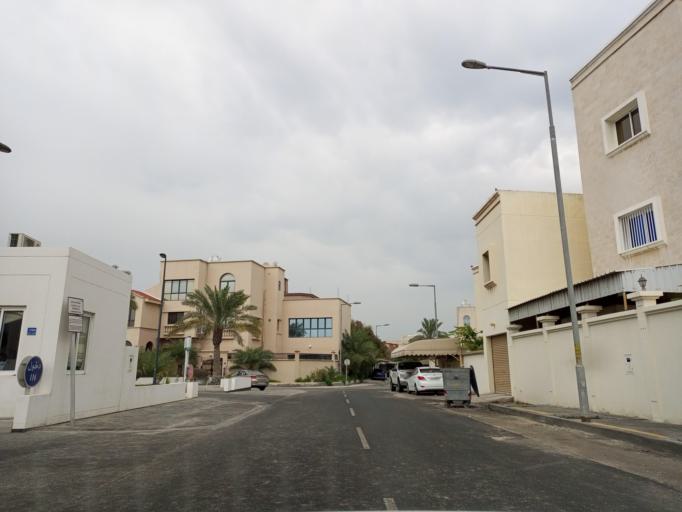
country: BH
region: Muharraq
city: Al Hadd
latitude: 26.2618
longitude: 50.6372
